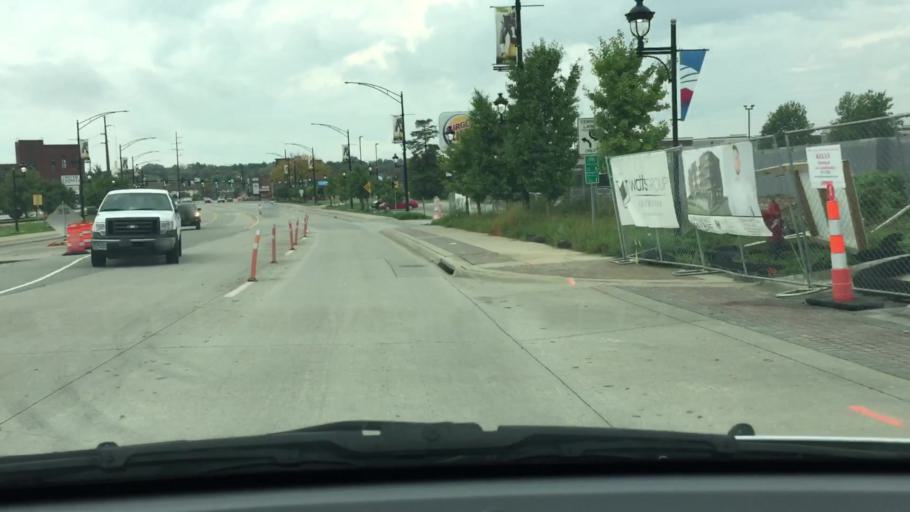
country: US
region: Iowa
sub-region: Johnson County
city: Coralville
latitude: 41.6758
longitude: -91.5662
